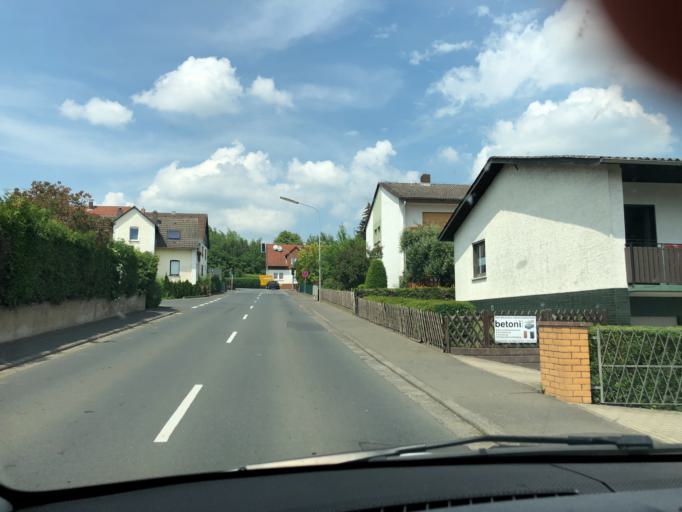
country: DE
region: Hesse
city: Neustadt (Hessen)
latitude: 50.8507
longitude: 9.1088
